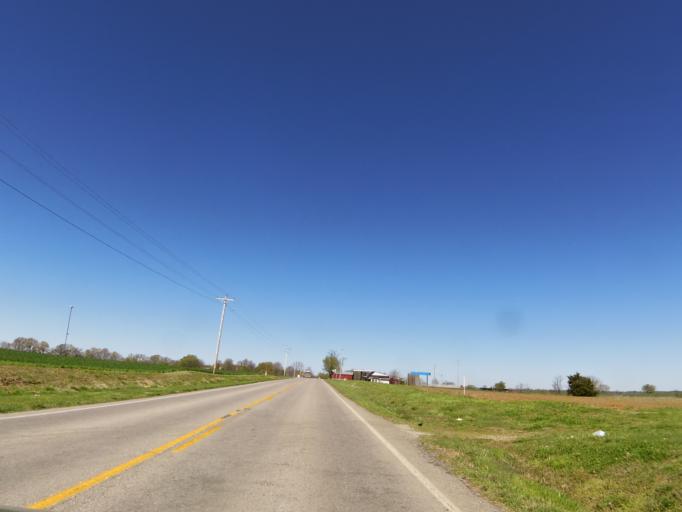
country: US
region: Kentucky
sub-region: Logan County
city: Russellville
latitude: 36.6814
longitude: -86.8553
